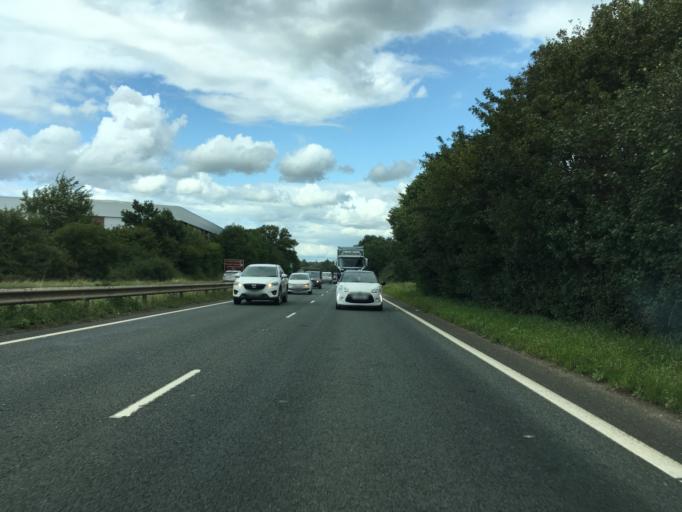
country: GB
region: England
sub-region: Gloucestershire
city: Gloucester
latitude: 51.8284
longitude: -2.2728
